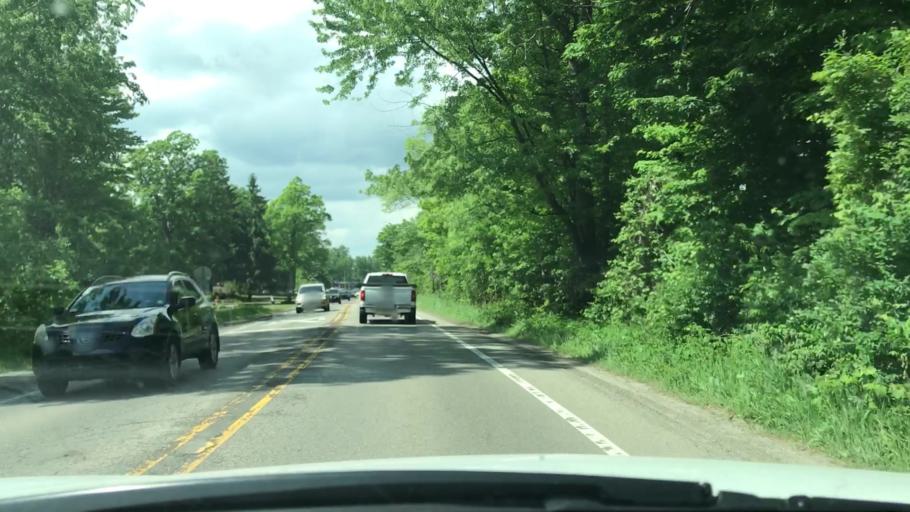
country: US
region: Michigan
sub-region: Oakland County
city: Auburn Hills
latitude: 42.7205
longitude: -83.2846
